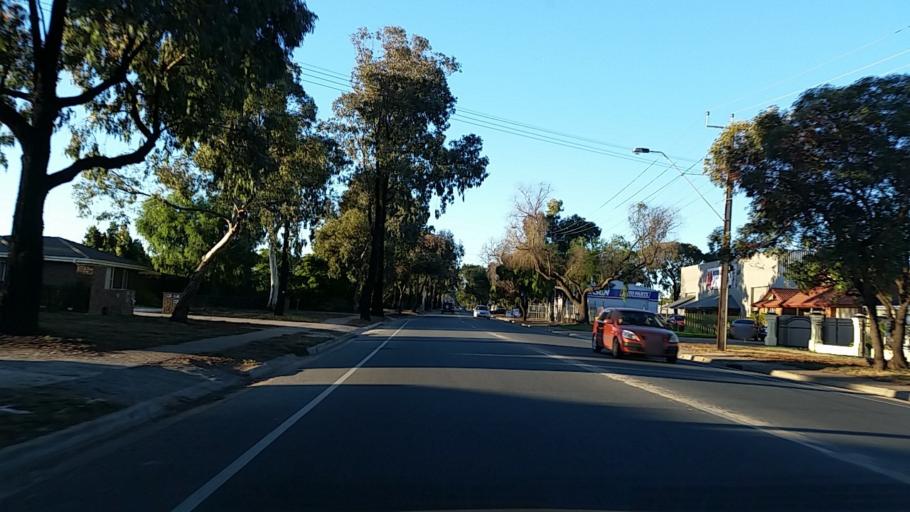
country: AU
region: South Australia
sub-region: Salisbury
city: Salisbury
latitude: -34.7675
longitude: 138.6527
